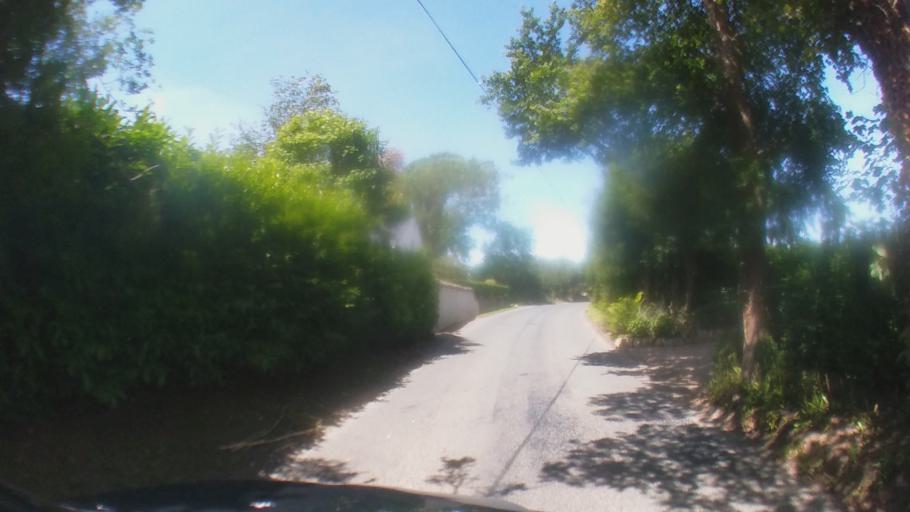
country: IE
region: Leinster
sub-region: Loch Garman
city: Loch Garman
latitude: 52.2332
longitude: -6.5641
